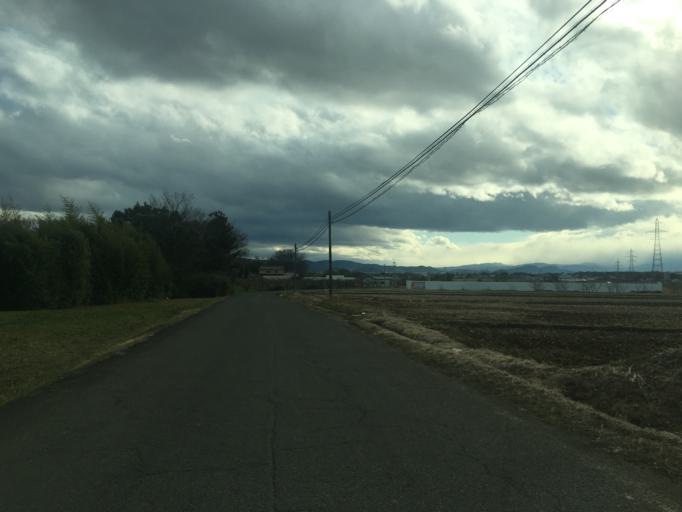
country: JP
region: Fukushima
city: Yanagawamachi-saiwaicho
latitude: 37.8860
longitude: 140.5763
